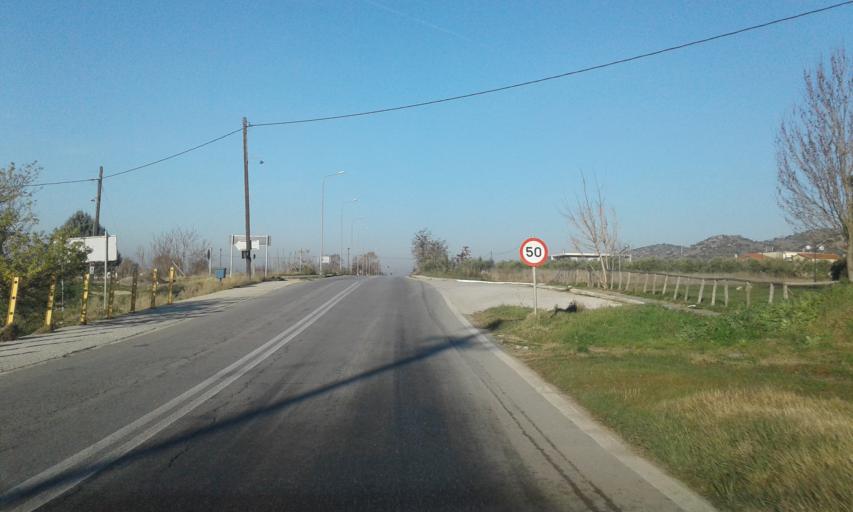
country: GR
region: Central Macedonia
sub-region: Nomos Thessalonikis
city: Gerakarou
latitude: 40.6920
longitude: 23.2202
